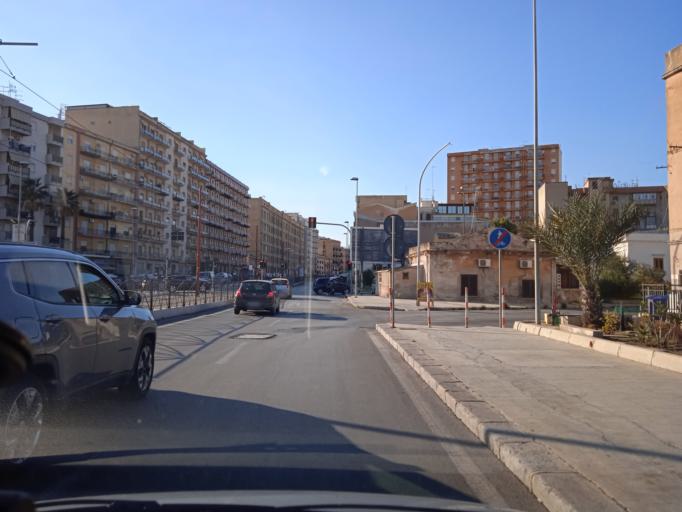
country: IT
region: Sicily
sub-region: Palermo
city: Ciaculli
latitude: 38.1065
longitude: 13.3740
